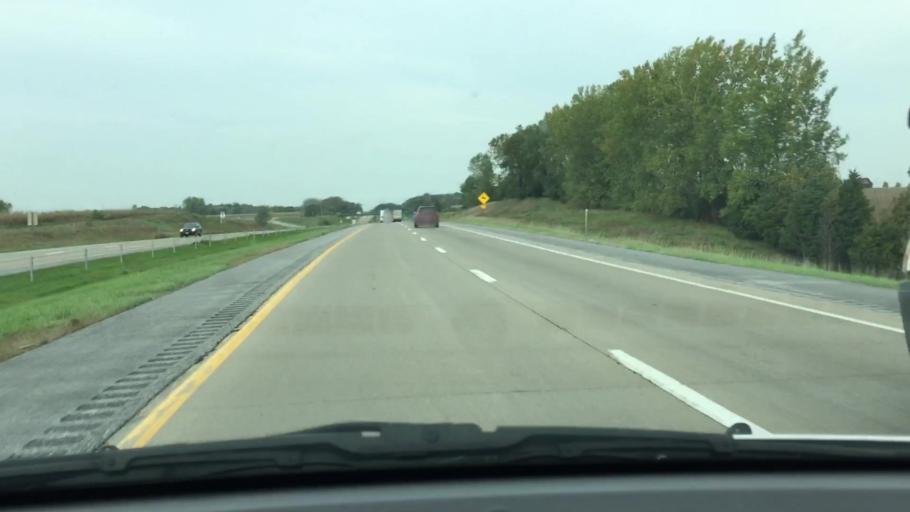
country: US
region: Iowa
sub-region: Muscatine County
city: Wilton
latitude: 41.6341
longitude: -91.0262
